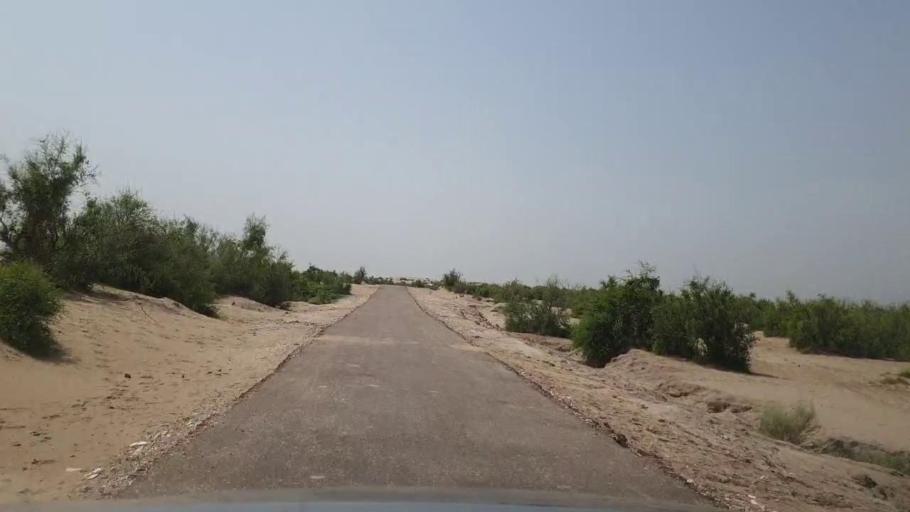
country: PK
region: Sindh
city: Pano Aqil
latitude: 27.6072
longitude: 69.1468
